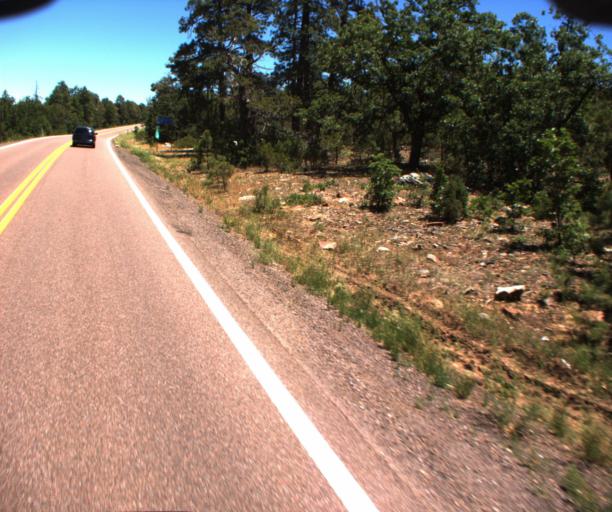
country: US
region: Arizona
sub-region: Gila County
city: Pine
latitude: 34.4330
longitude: -111.5060
